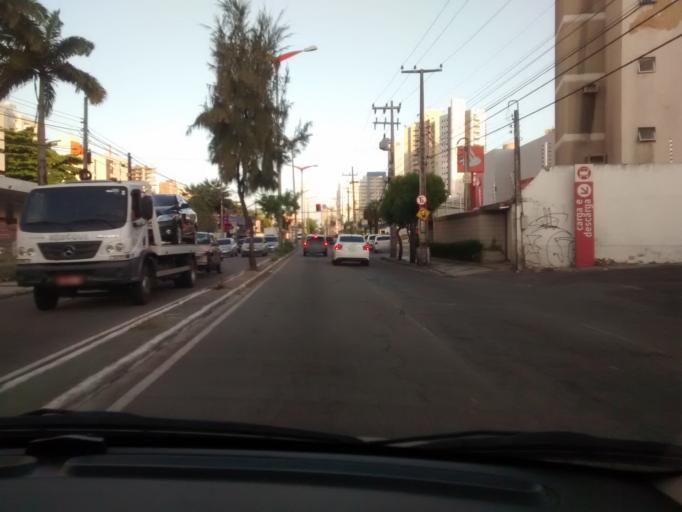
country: BR
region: Ceara
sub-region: Fortaleza
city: Fortaleza
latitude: -3.7421
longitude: -38.4805
